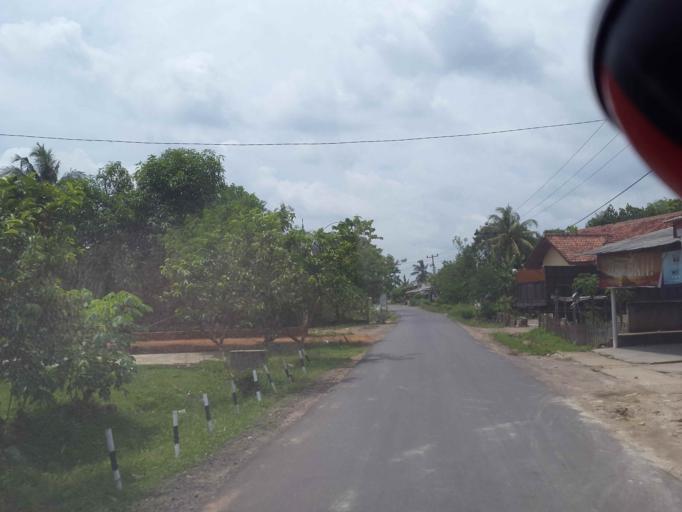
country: ID
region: Lampung
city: Natar
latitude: -5.2997
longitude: 105.2246
